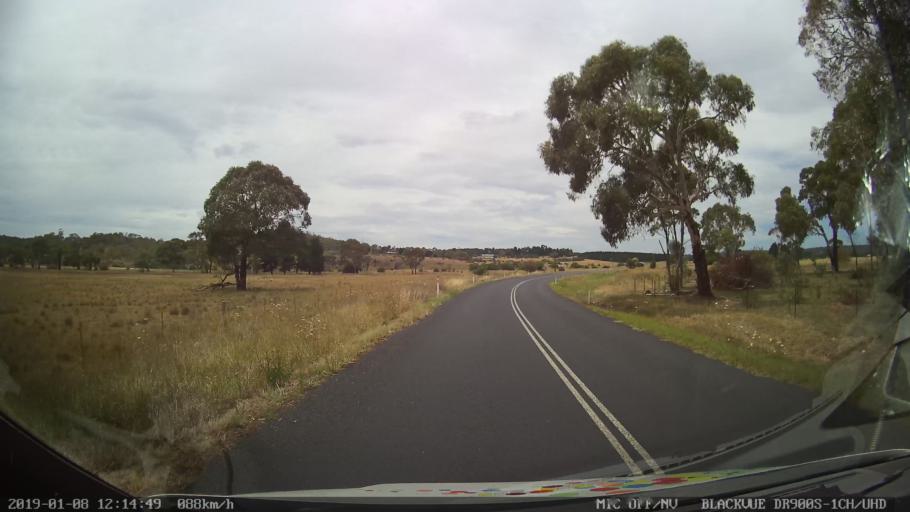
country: AU
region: New South Wales
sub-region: Armidale Dumaresq
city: Armidale
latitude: -30.4796
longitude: 151.6277
